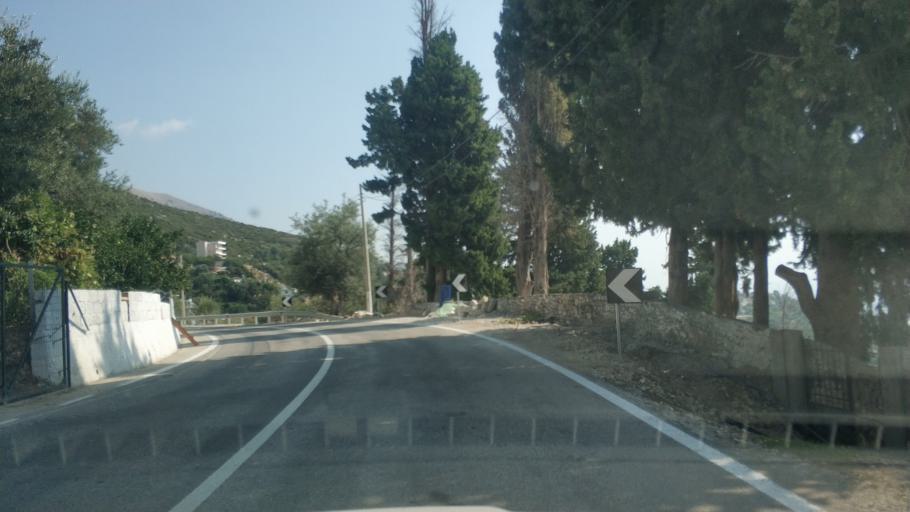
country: AL
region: Vlore
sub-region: Rrethi i Sarandes
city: Lukove
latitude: 40.0221
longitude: 19.8886
